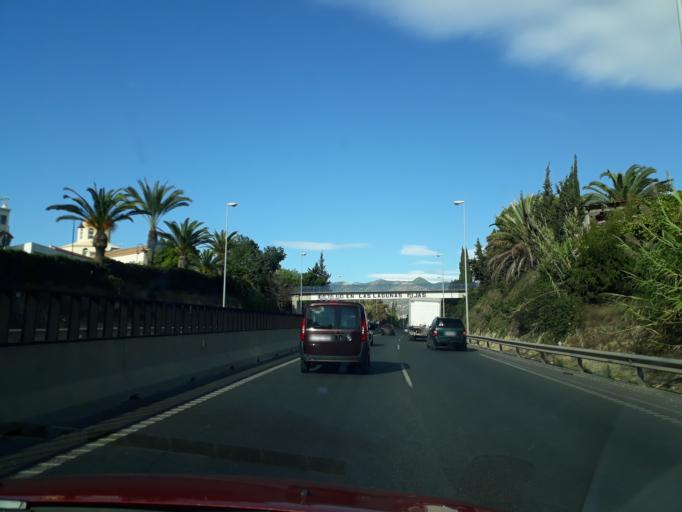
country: ES
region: Andalusia
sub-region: Provincia de Malaga
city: Fuengirola
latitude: 36.5424
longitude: -4.6347
